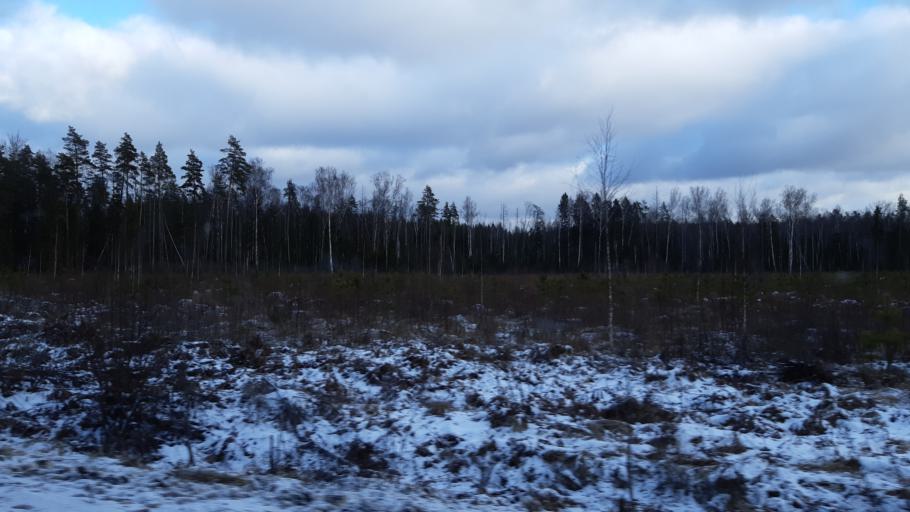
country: RU
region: Moskovskaya
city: Noginsk-9
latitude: 55.9691
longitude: 38.5369
